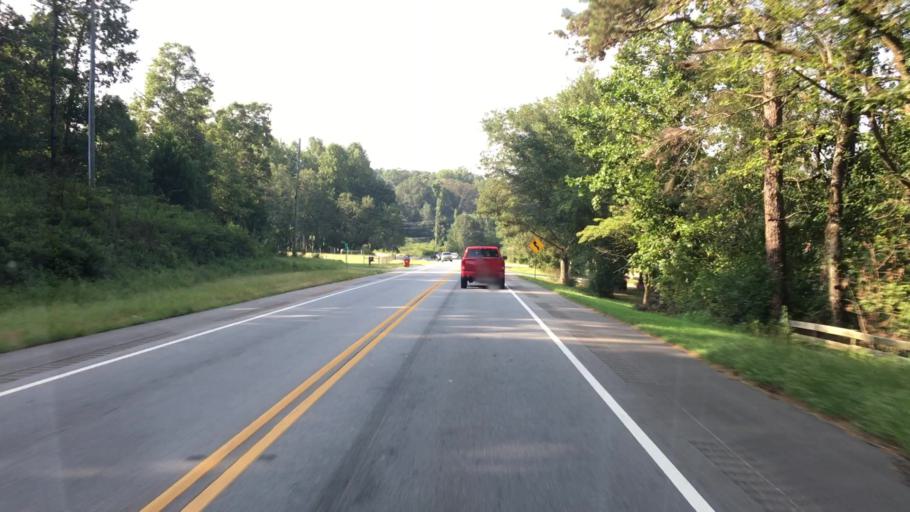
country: US
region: Georgia
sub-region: Barrow County
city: Winder
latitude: 34.0404
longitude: -83.7151
